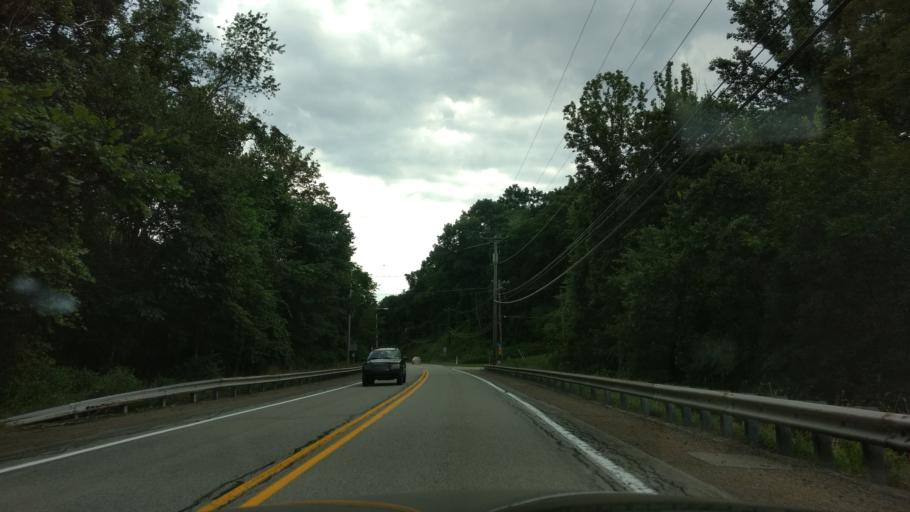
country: US
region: Pennsylvania
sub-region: Allegheny County
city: Plum
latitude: 40.4814
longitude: -79.7043
